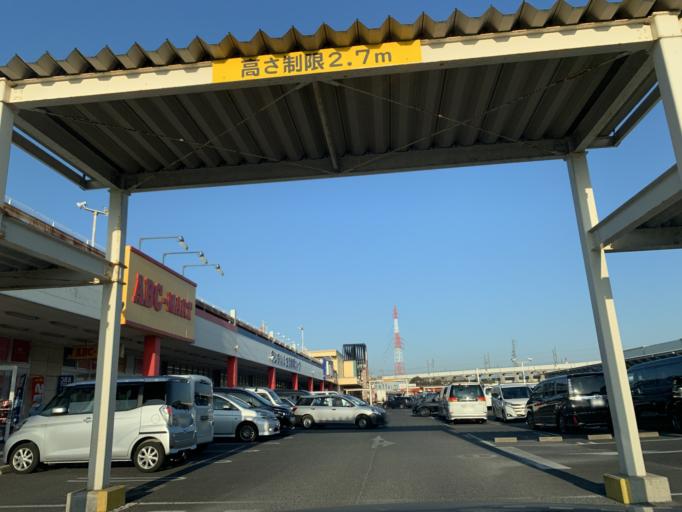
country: JP
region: Chiba
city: Funabashi
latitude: 35.6950
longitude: 139.9524
